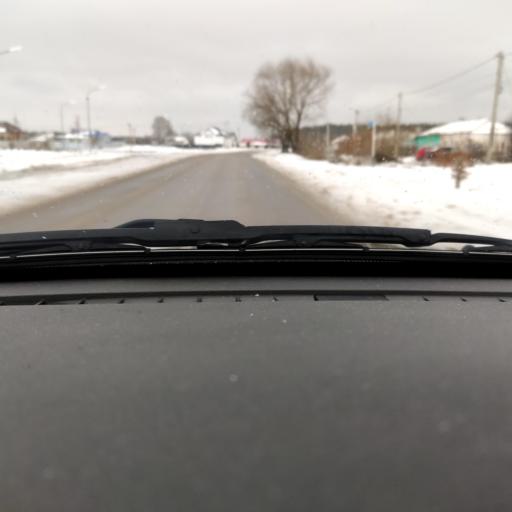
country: RU
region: Voronezj
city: Ramon'
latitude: 51.9056
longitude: 39.2858
